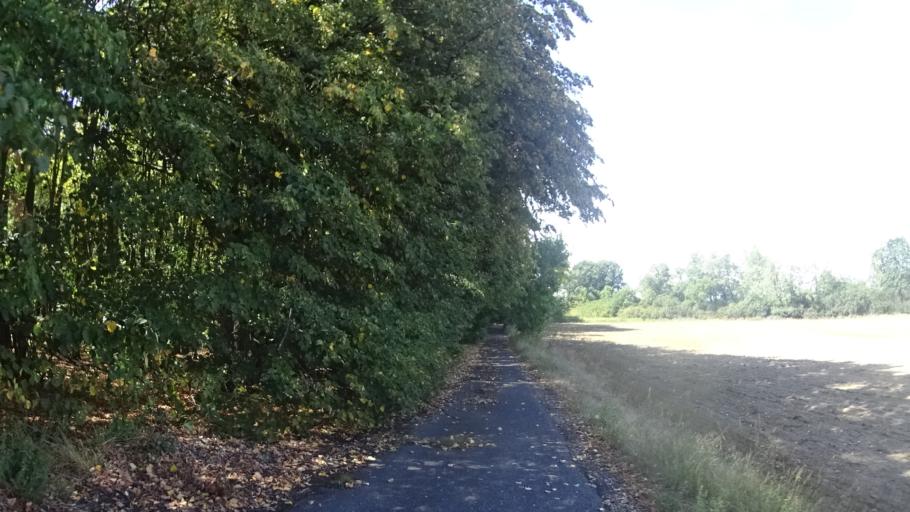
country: AT
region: Lower Austria
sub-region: Politischer Bezirk Ganserndorf
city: Angern an der March
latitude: 48.3560
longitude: 16.8820
